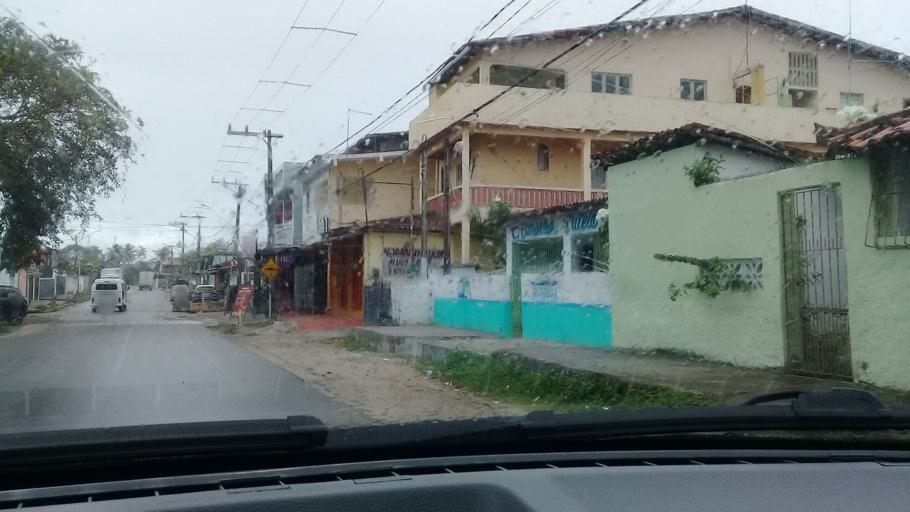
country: BR
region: Pernambuco
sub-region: Itamaraca
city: Itamaraca
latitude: -7.7345
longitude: -34.8260
